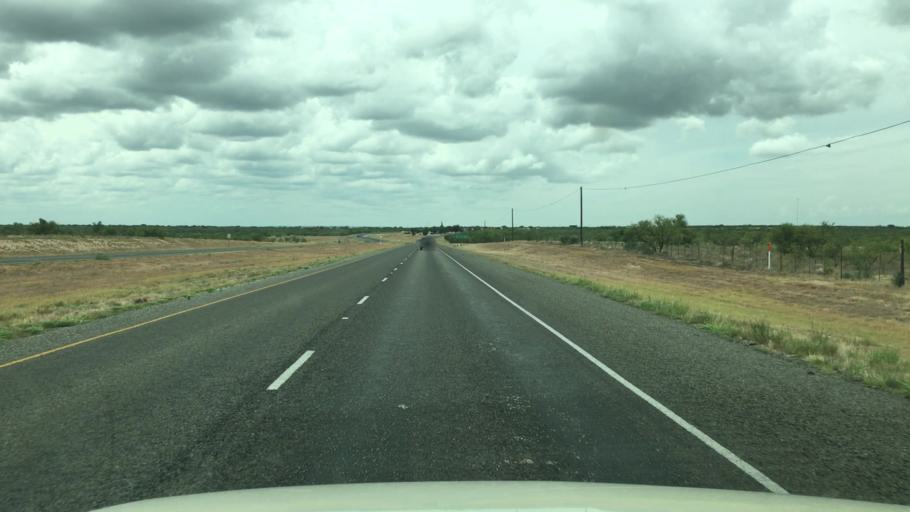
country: US
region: Texas
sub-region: Concho County
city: Eden
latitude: 31.2175
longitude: -99.9494
